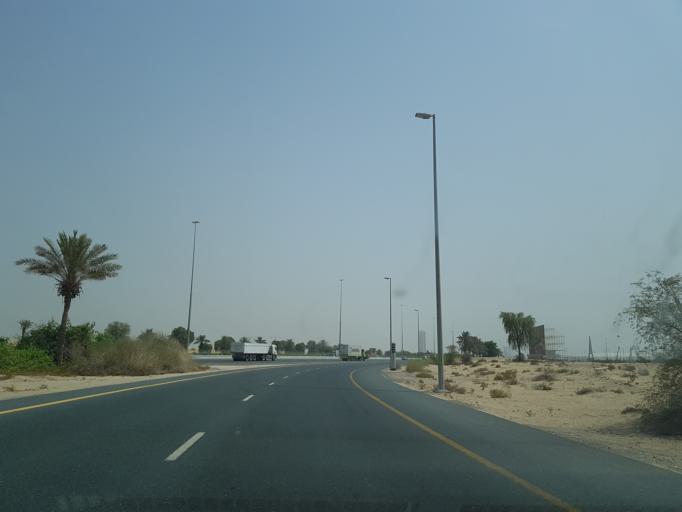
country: AE
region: Dubai
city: Dubai
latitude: 25.0661
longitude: 55.2966
